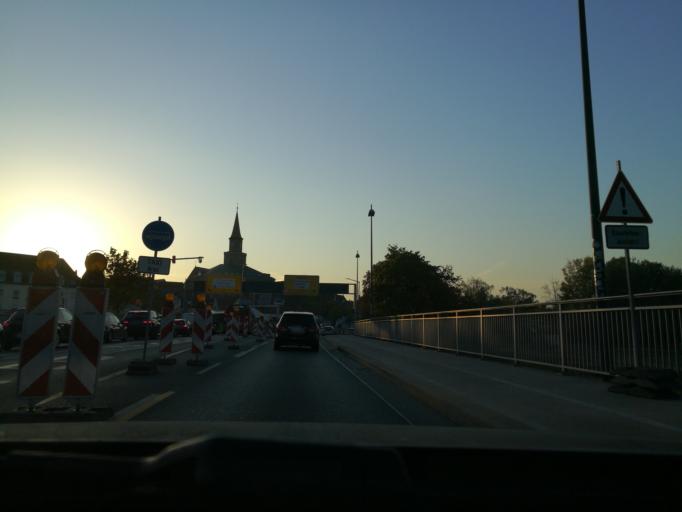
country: DE
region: Bavaria
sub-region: Regierungsbezirk Mittelfranken
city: Furth
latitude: 49.4802
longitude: 10.9919
